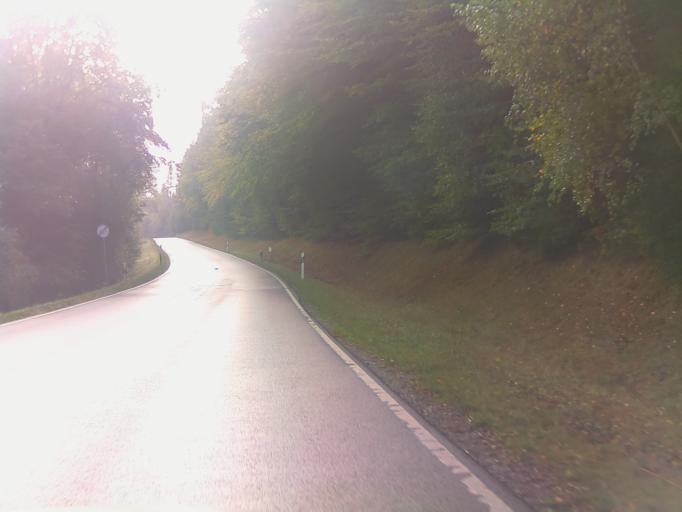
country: DE
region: Hesse
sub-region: Regierungsbezirk Kassel
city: Hosenfeld
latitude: 50.5057
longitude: 9.5361
